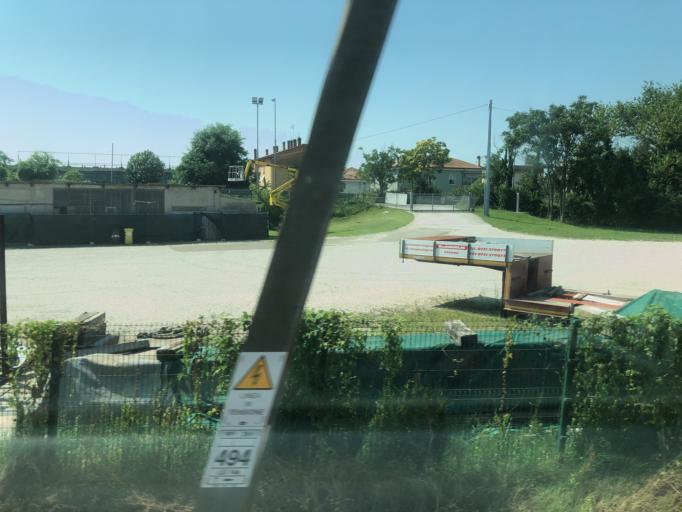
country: IT
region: The Marches
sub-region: Provincia di Pesaro e Urbino
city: Pesaro
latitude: 43.9096
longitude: 12.8704
